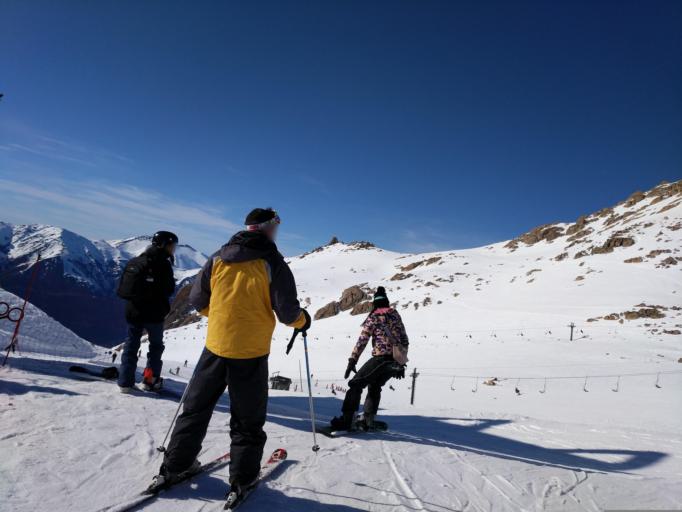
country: AR
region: Rio Negro
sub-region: Departamento de Bariloche
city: San Carlos de Bariloche
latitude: -41.1748
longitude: -71.4736
